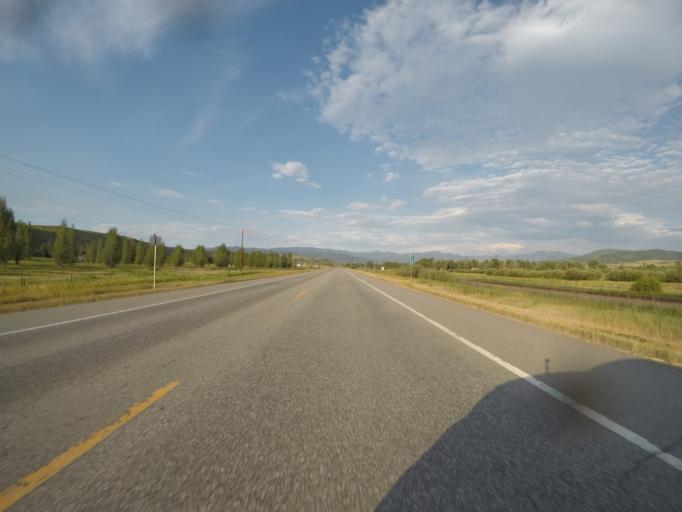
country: US
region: Colorado
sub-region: Routt County
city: Steamboat Springs
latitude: 40.4920
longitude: -106.9544
